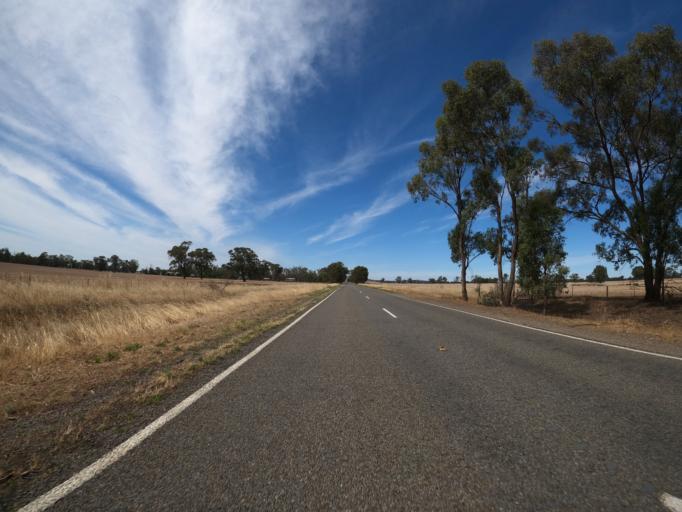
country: AU
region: Victoria
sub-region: Benalla
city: Benalla
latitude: -36.2884
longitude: 145.9523
